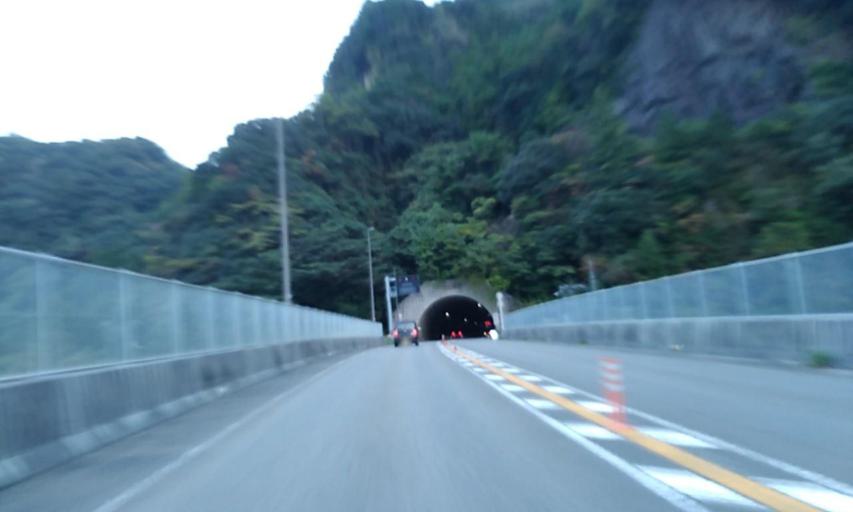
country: JP
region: Wakayama
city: Shingu
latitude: 33.7210
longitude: 135.9736
